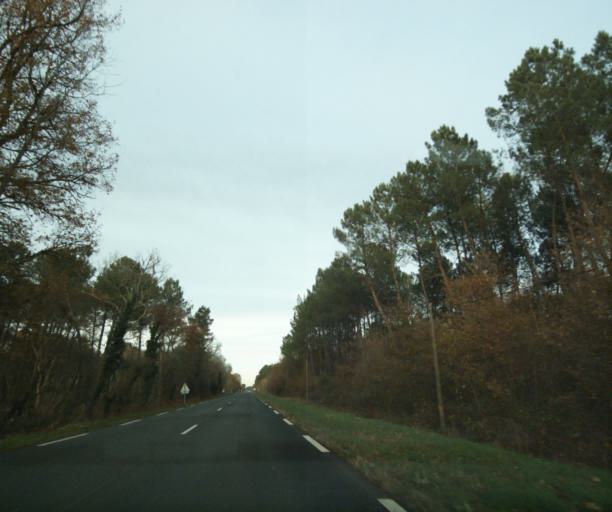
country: FR
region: Aquitaine
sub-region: Departement de la Gironde
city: Bazas
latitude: 44.3042
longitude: -0.2541
